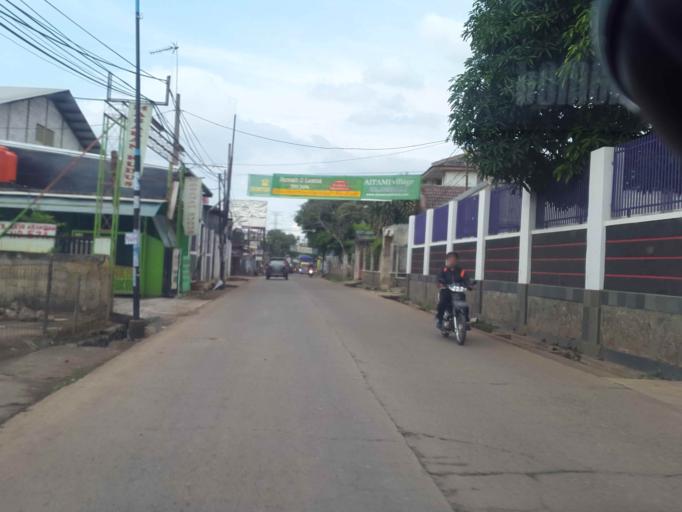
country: ID
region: West Java
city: Cileungsir
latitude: -6.3622
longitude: 106.9206
